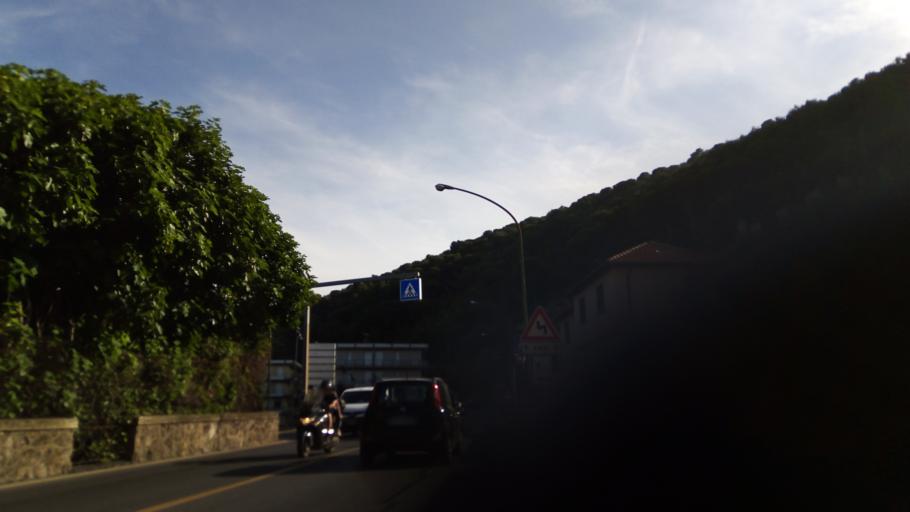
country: IT
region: Liguria
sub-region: Provincia di Savona
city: Borghetto Santo Spirito
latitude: 44.1079
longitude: 8.2398
